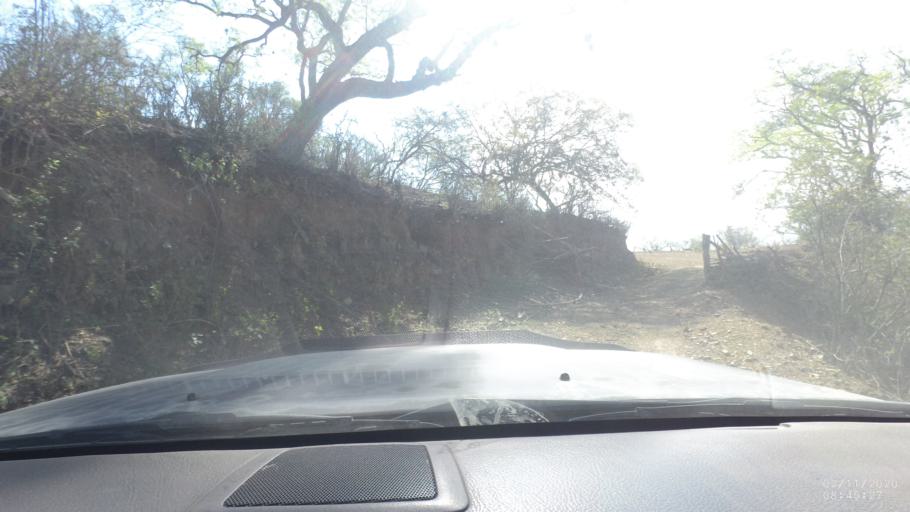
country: BO
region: Chuquisaca
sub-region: Provincia Zudanez
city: Mojocoya
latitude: -18.5679
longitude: -64.5475
